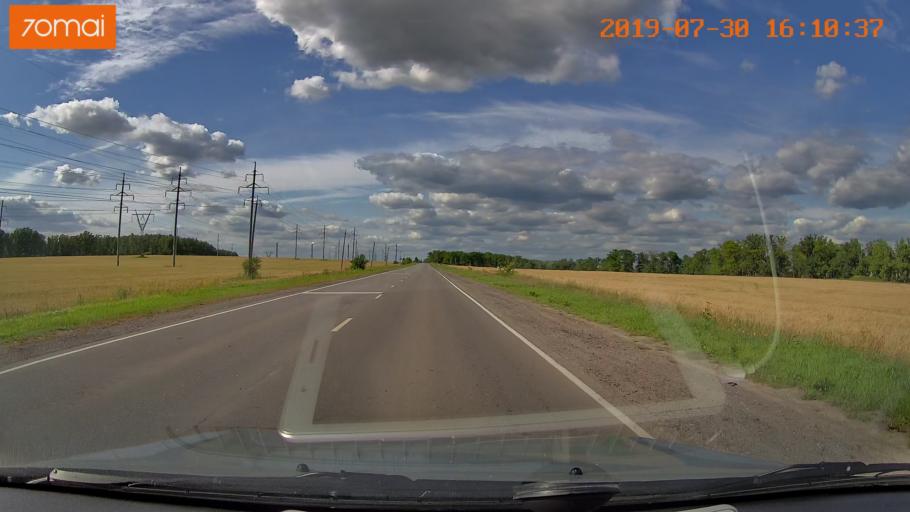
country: RU
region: Moskovskaya
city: Peski
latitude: 55.2647
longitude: 38.7153
